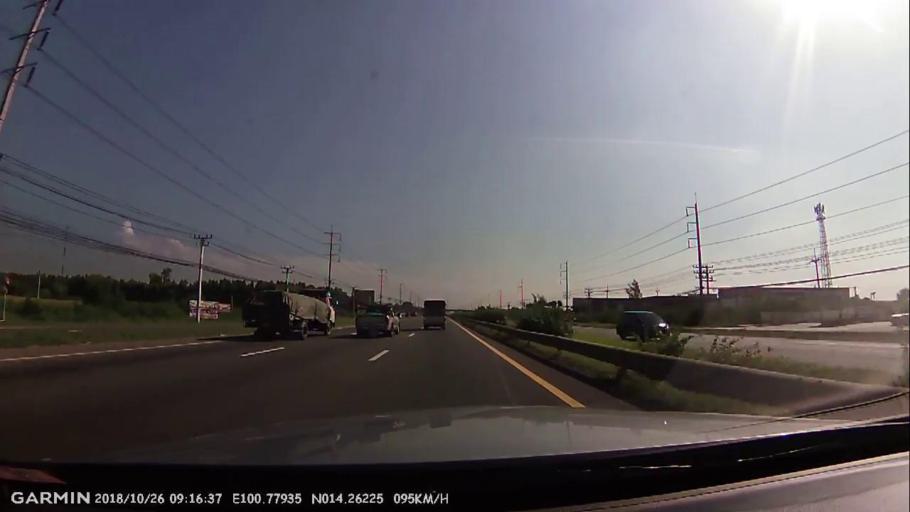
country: TH
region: Phra Nakhon Si Ayutthaya
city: Wang Noi
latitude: 14.2626
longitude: 100.7793
